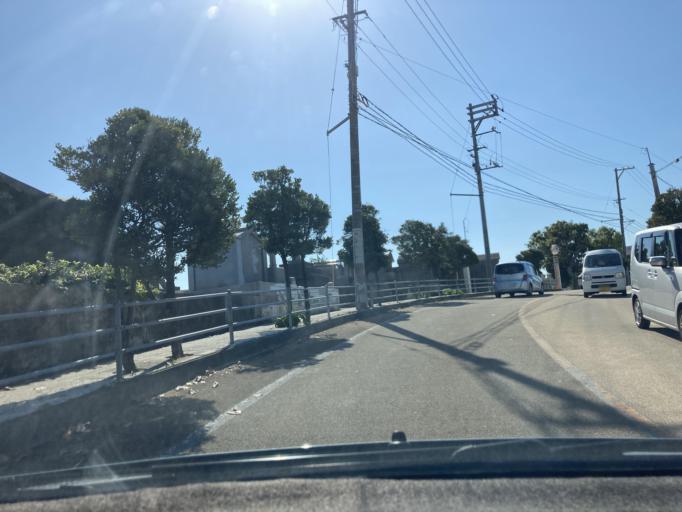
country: JP
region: Okinawa
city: Naha-shi
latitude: 26.2083
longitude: 127.7156
